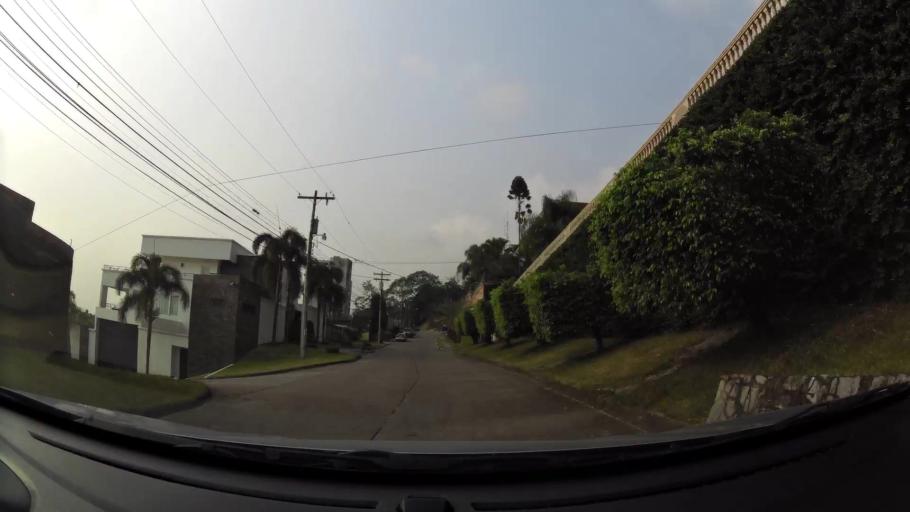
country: HN
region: Cortes
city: Armenta
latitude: 15.4994
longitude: -88.0513
